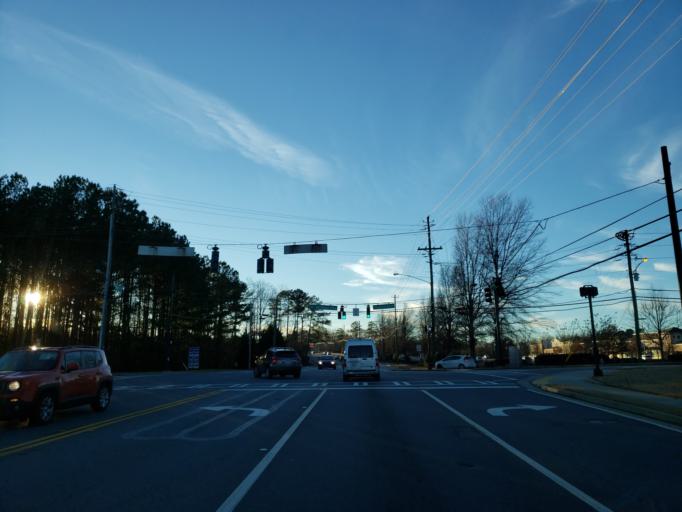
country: US
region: Georgia
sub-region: Fulton County
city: Alpharetta
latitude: 34.0922
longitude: -84.2852
